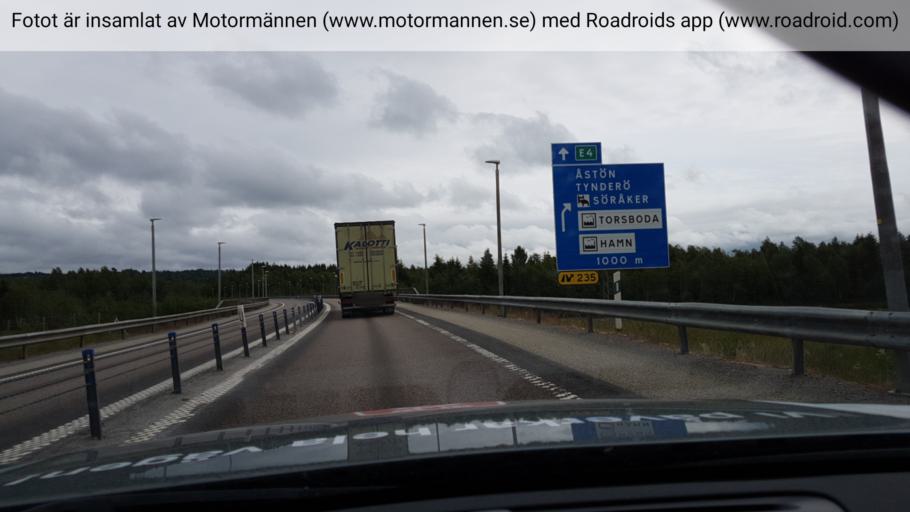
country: SE
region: Vaesternorrland
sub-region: Timra Kommun
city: Soraker
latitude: 62.5168
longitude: 17.4526
